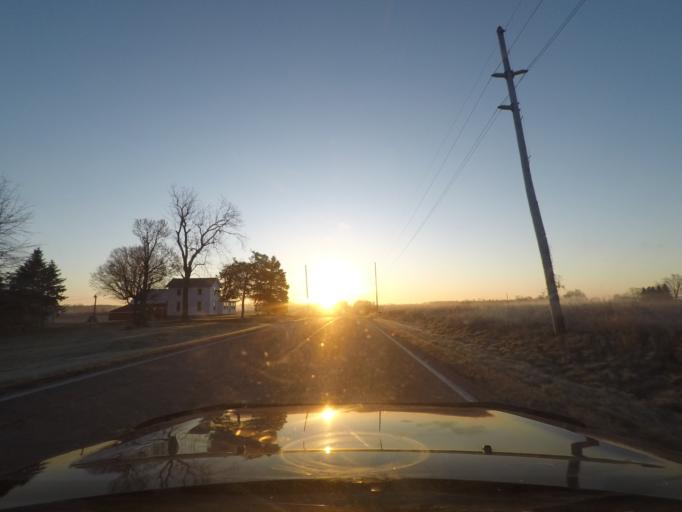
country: US
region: Indiana
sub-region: Saint Joseph County
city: Walkerton
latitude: 41.4478
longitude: -86.4339
